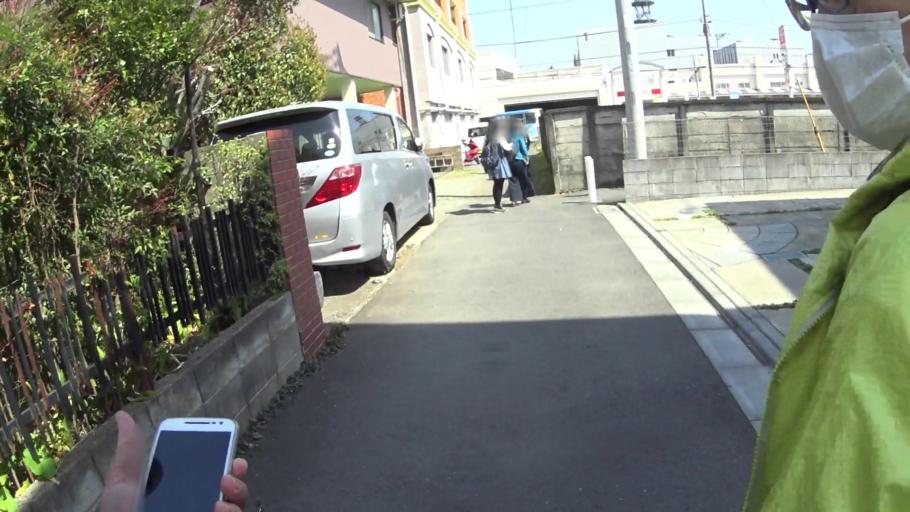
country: JP
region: Tokyo
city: Kokubunji
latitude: 35.7085
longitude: 139.4865
